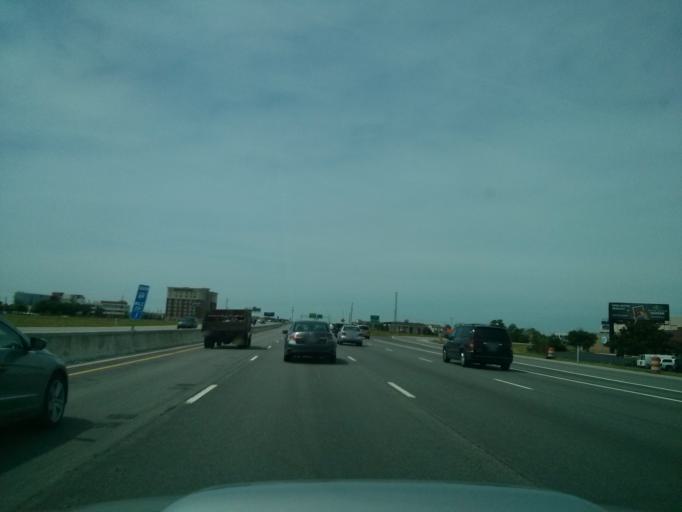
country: US
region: Indiana
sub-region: Hamilton County
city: Fishers
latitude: 39.9088
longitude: -86.0431
